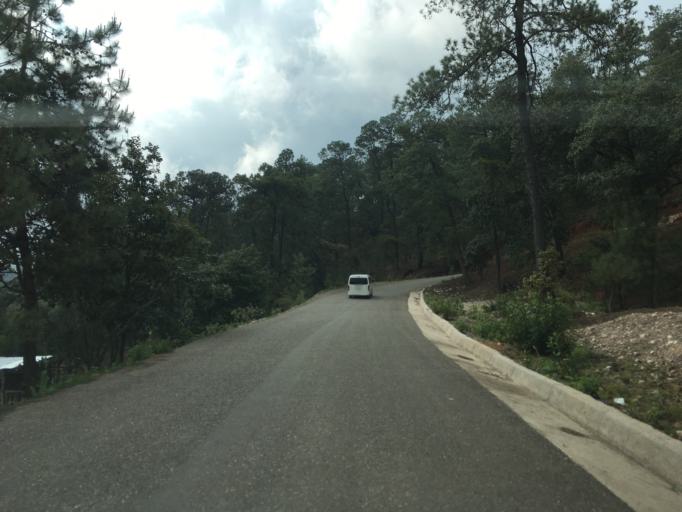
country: MX
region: Oaxaca
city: Santiago Tilantongo
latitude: 17.2130
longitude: -97.2797
